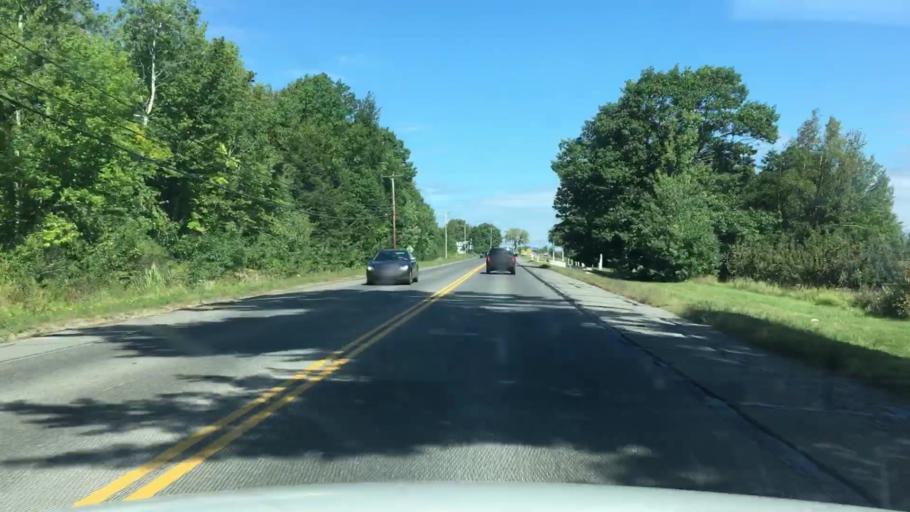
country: US
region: Maine
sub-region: Penobscot County
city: Newport
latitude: 44.8569
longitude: -69.2838
